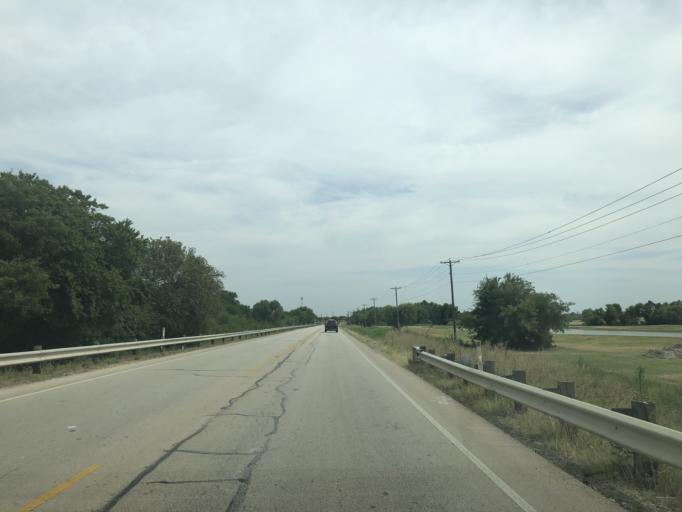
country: US
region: Texas
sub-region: Tarrant County
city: Blue Mound
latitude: 32.8888
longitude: -97.3453
